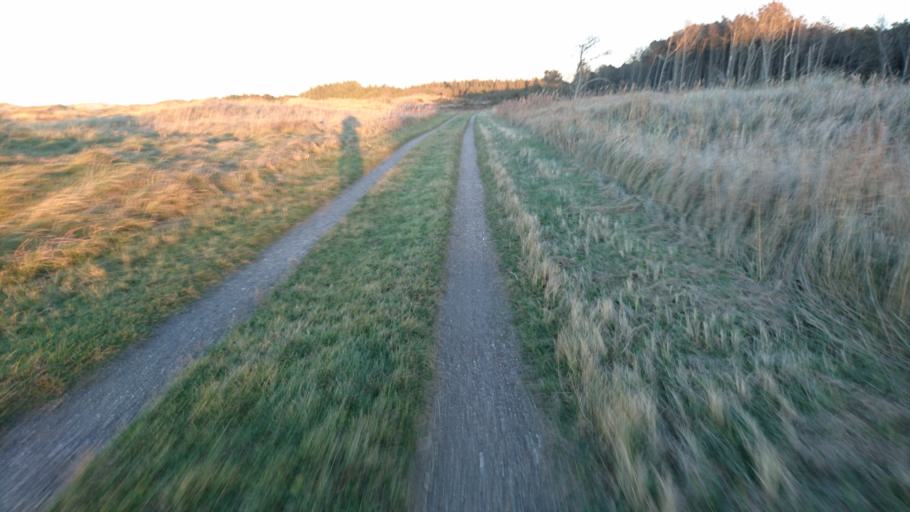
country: DK
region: North Denmark
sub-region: Frederikshavn Kommune
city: Skagen
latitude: 57.7122
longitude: 10.4971
